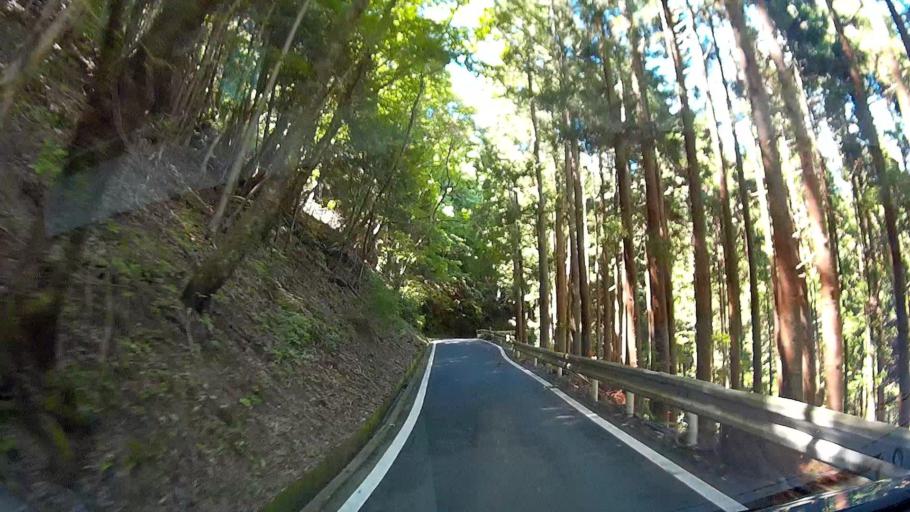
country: JP
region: Shizuoka
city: Shizuoka-shi
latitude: 35.1907
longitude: 138.2653
